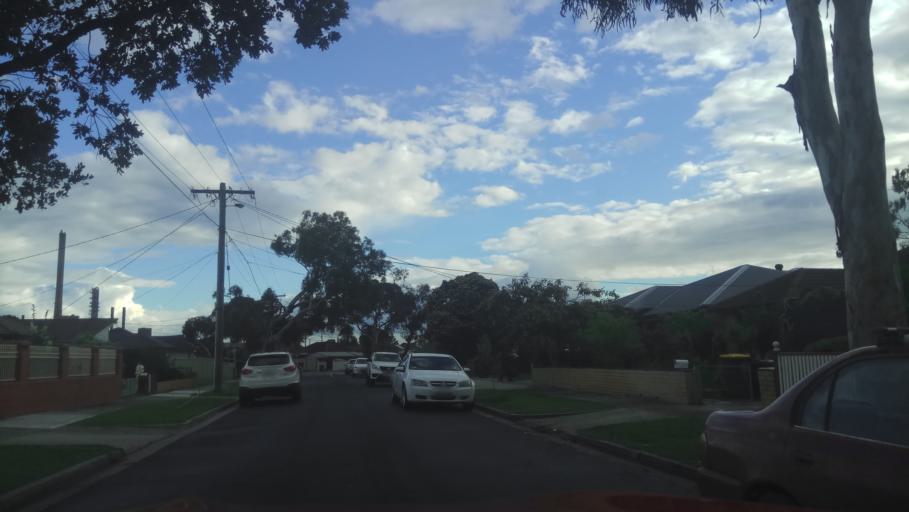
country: AU
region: Victoria
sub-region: Hobsons Bay
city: Altona North
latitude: -37.8441
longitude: 144.8471
